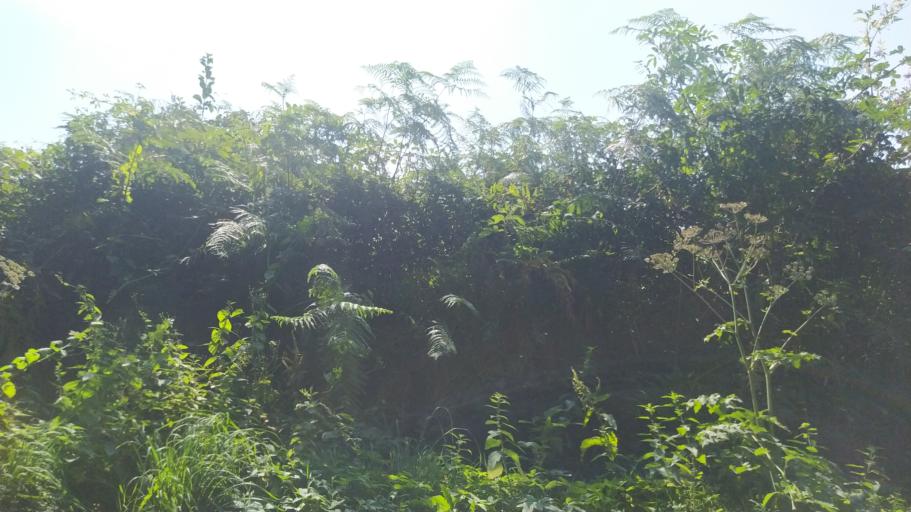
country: GB
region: England
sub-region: Hampshire
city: Cadnam
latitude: 50.9289
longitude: -1.5392
